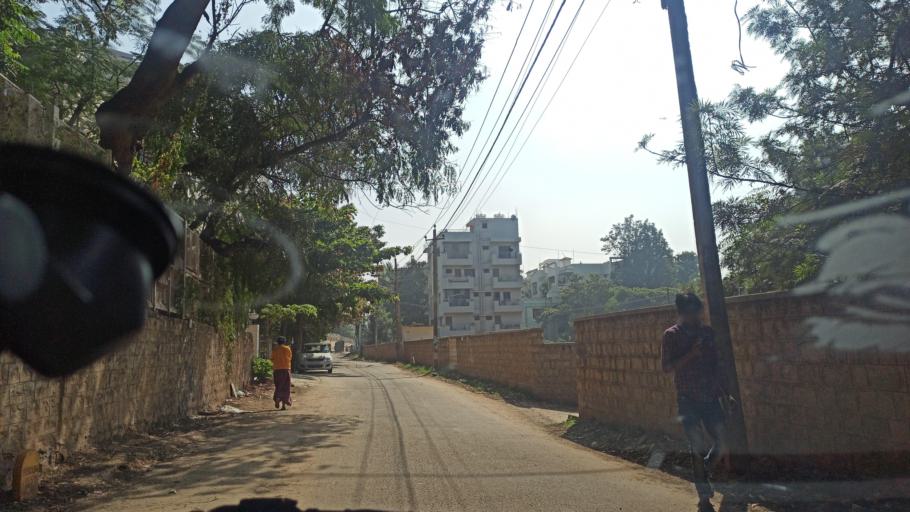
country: IN
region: Karnataka
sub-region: Bangalore Urban
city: Yelahanka
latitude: 13.0681
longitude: 77.5884
